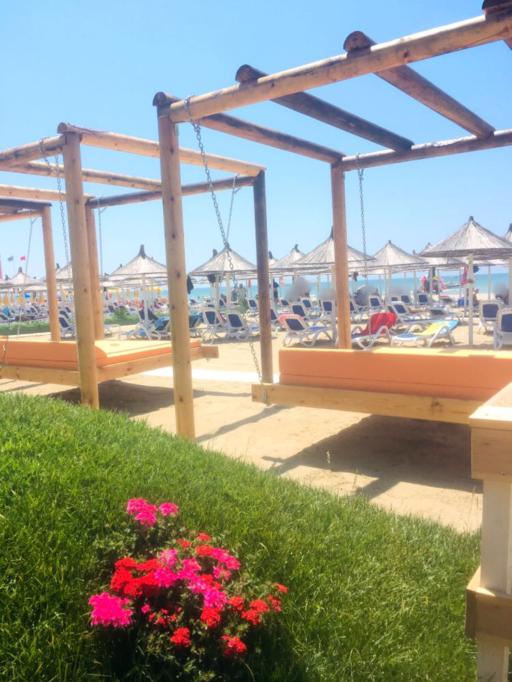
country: AL
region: Tirane
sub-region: Rrethi i Kavajes
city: Golem
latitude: 41.2602
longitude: 19.5218
